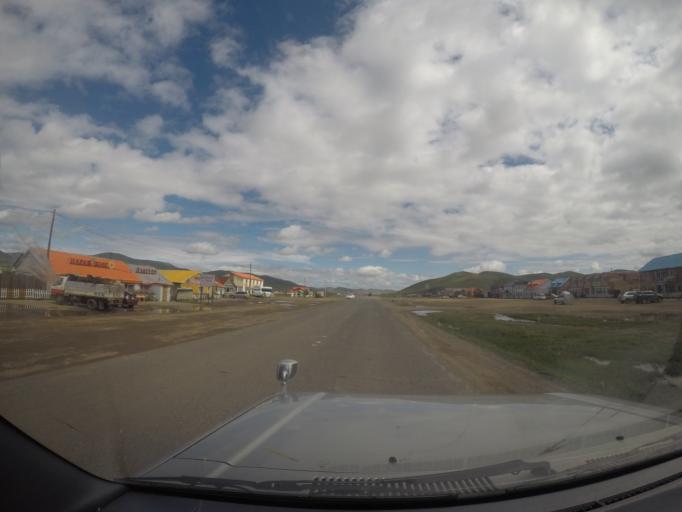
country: MN
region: Hentiy
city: Modot
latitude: 47.7236
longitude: 109.0271
